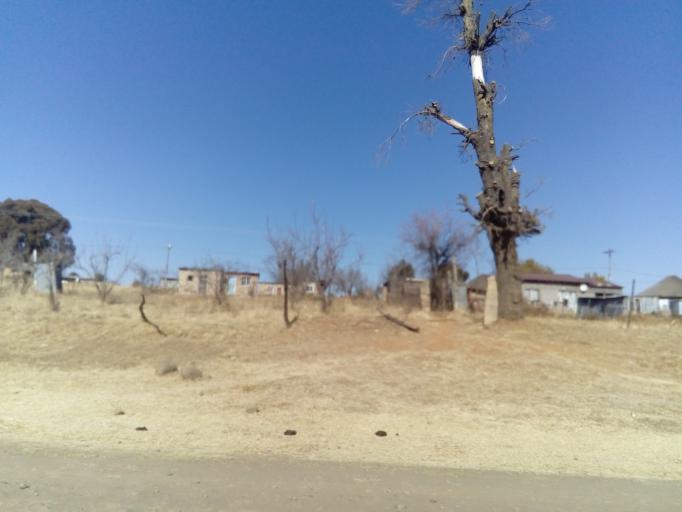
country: LS
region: Berea
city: Teyateyaneng
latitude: -29.1240
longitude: 27.8287
